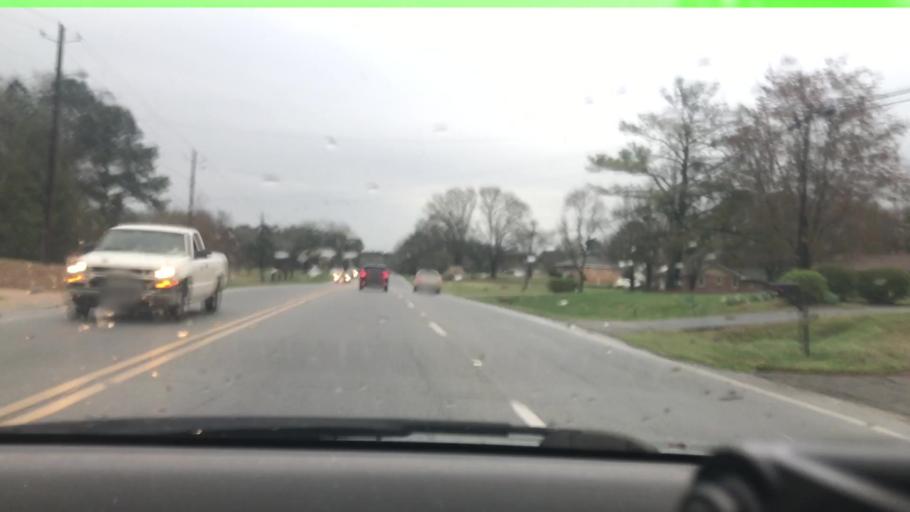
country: US
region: Georgia
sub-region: Oglethorpe County
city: Lexington
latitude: 33.8853
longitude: -83.1465
